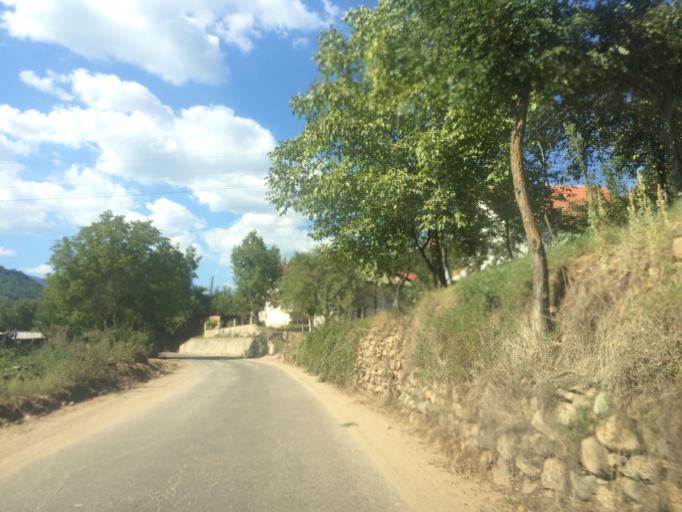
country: MK
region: Makedonska Kamenica
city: Makedonska Kamenica
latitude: 42.0400
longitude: 22.5788
